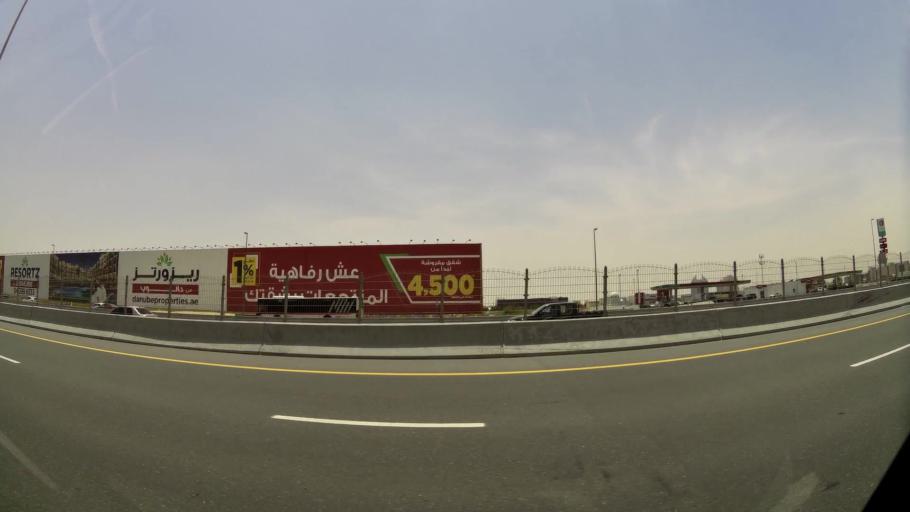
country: AE
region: Ash Shariqah
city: Sharjah
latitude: 25.1343
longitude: 55.3794
